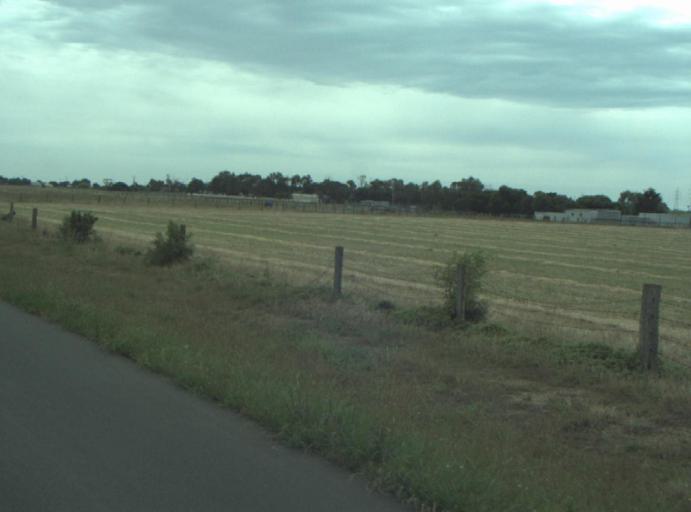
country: AU
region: Victoria
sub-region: Greater Geelong
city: Breakwater
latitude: -38.1933
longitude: 144.3989
